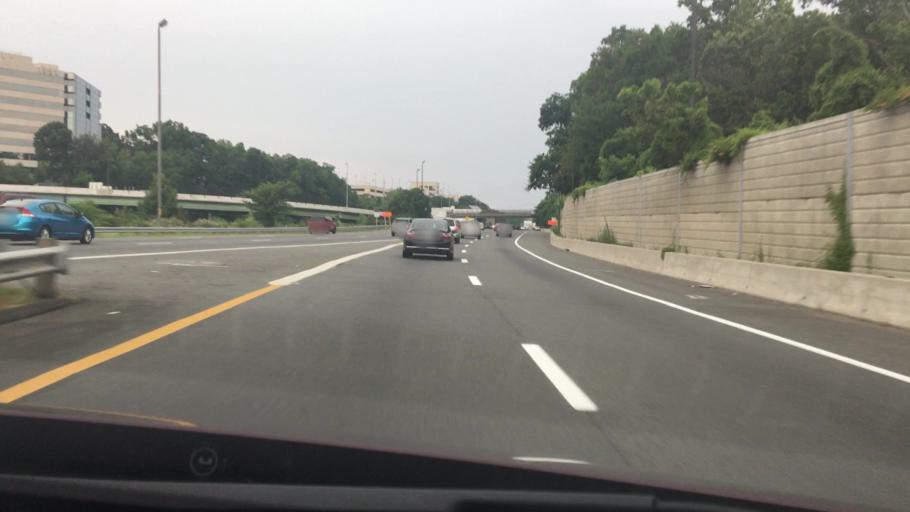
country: US
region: Virginia
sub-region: Fairfax County
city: Dunn Loring
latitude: 38.8854
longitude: -77.2242
